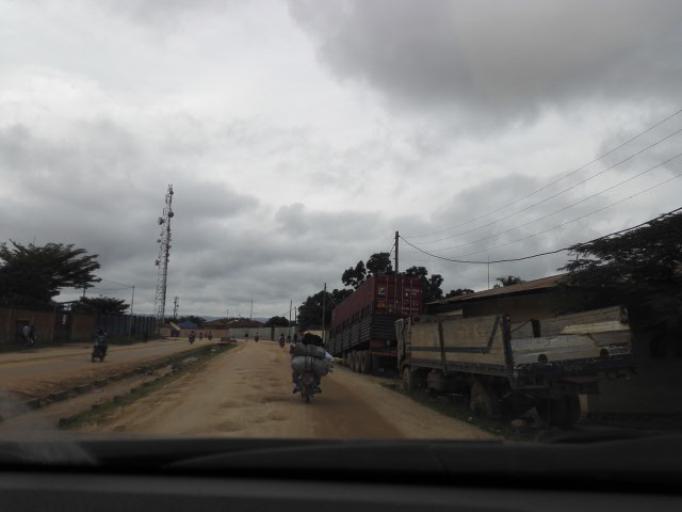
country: CD
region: Eastern Province
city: Bunia
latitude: 1.5504
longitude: 30.2488
